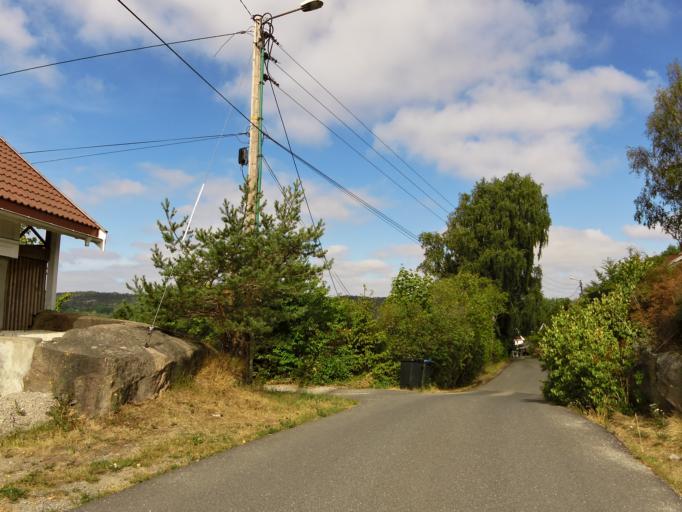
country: NO
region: Ostfold
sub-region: Fredrikstad
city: Fredrikstad
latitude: 59.2370
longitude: 10.9170
